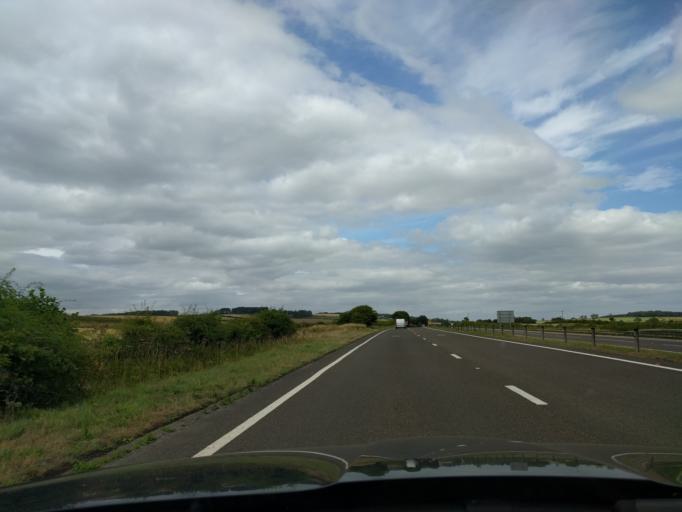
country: GB
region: England
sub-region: Northumberland
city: Alnwick
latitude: 55.4247
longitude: -1.6857
